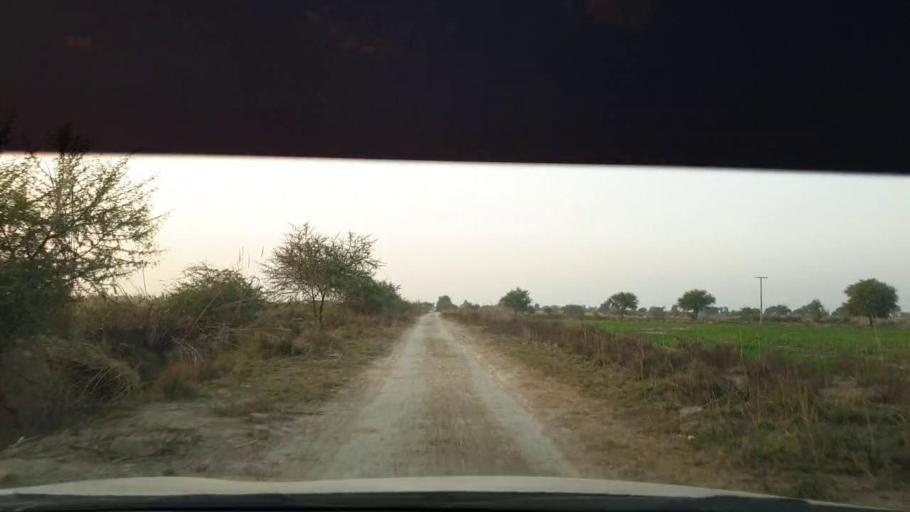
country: PK
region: Sindh
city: Berani
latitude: 25.7715
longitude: 68.9782
